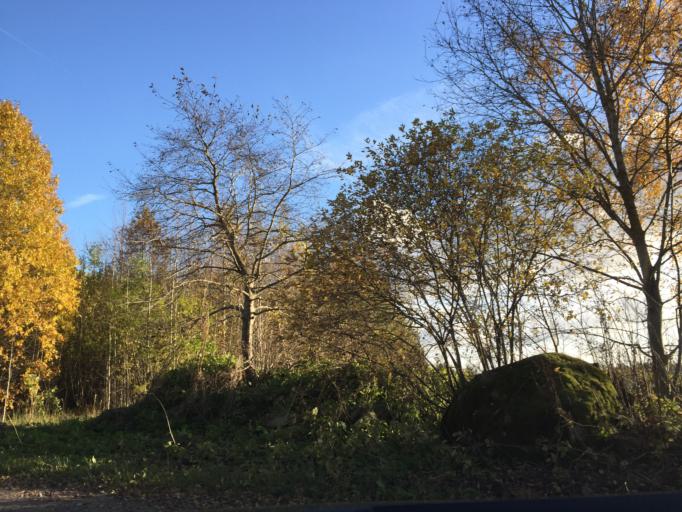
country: LV
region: Ogre
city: Jumprava
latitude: 56.7615
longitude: 24.9949
